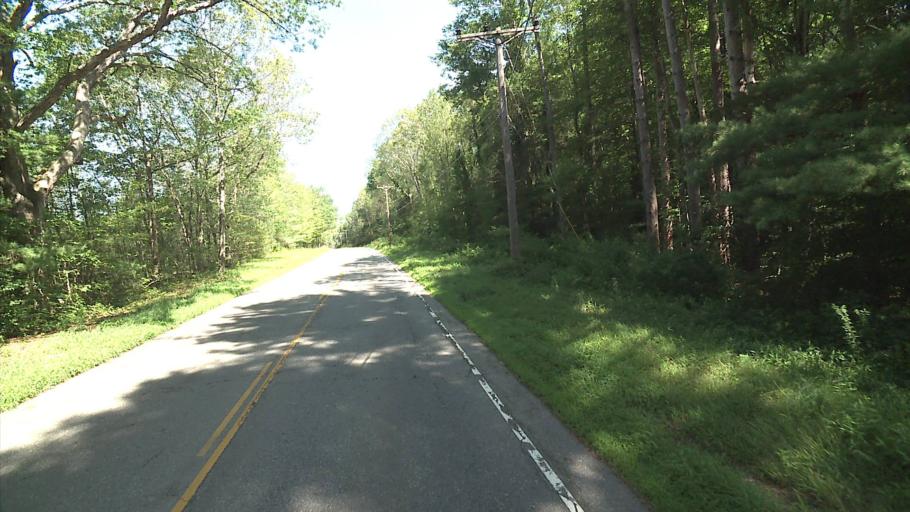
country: US
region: Connecticut
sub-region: New London County
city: Baltic
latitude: 41.6808
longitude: -72.0845
